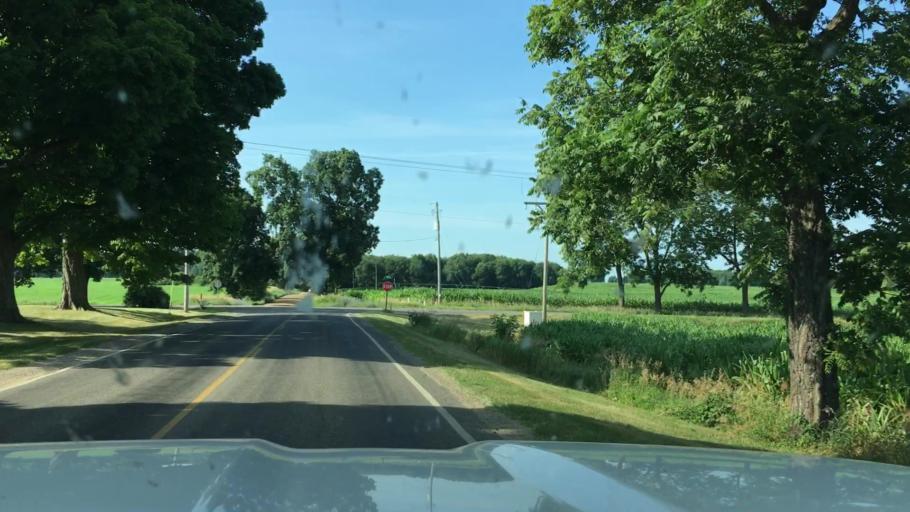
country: US
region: Michigan
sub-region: Barry County
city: Stony Point
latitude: 42.4576
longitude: -85.4447
